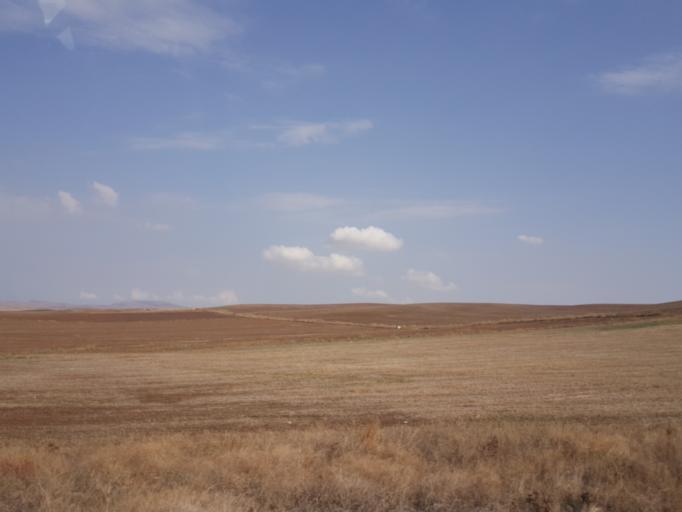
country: TR
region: Corum
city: Alaca
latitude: 40.1566
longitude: 34.8740
